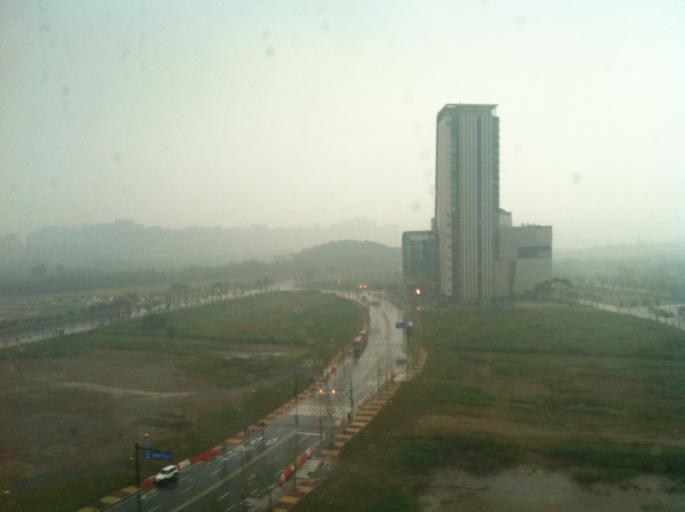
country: KR
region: Gyeonggi-do
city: Goyang-si
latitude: 37.6619
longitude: 126.7512
